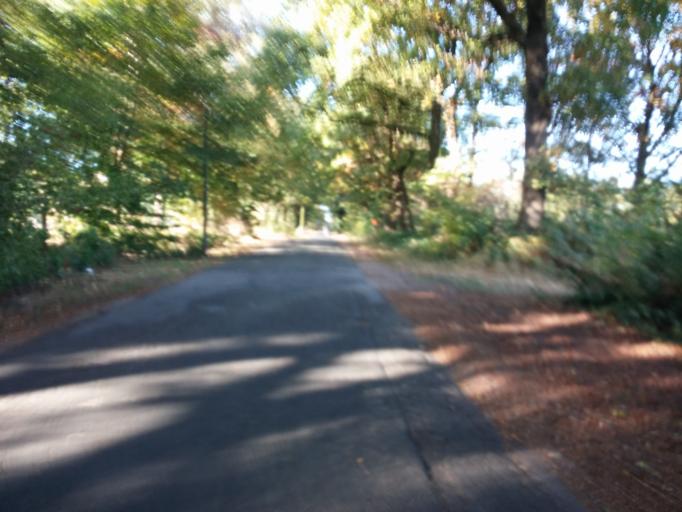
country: DE
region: North Rhine-Westphalia
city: Dorsten
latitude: 51.6395
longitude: 6.9780
